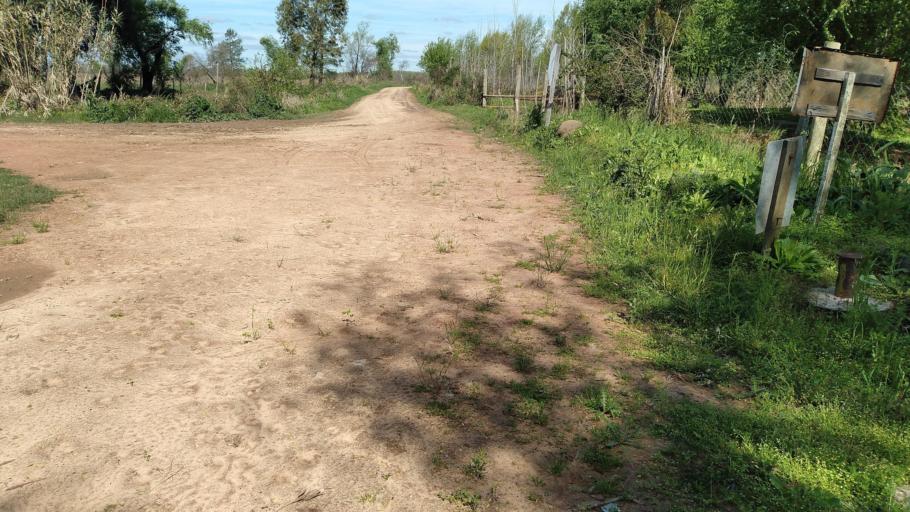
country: AR
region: Entre Rios
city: Villa Paranacito
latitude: -33.7142
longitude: -58.6500
